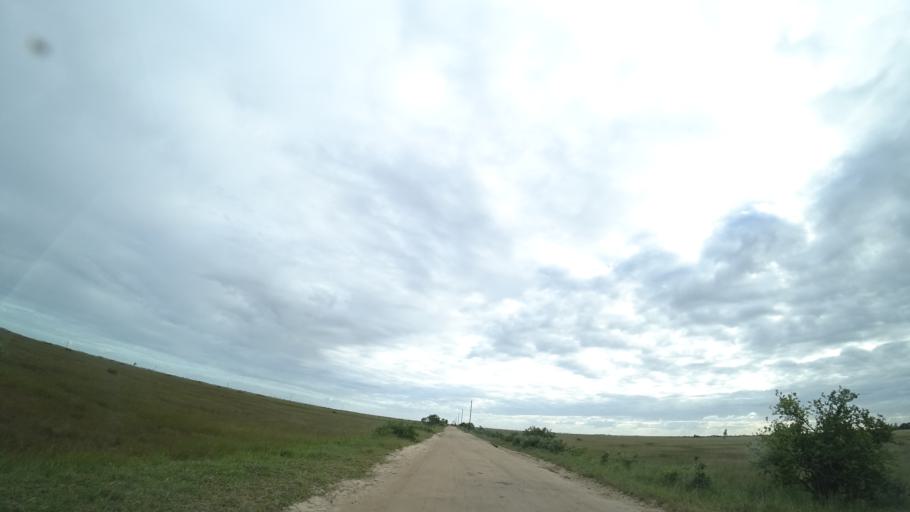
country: MZ
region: Sofala
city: Beira
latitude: -19.7410
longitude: 34.9629
